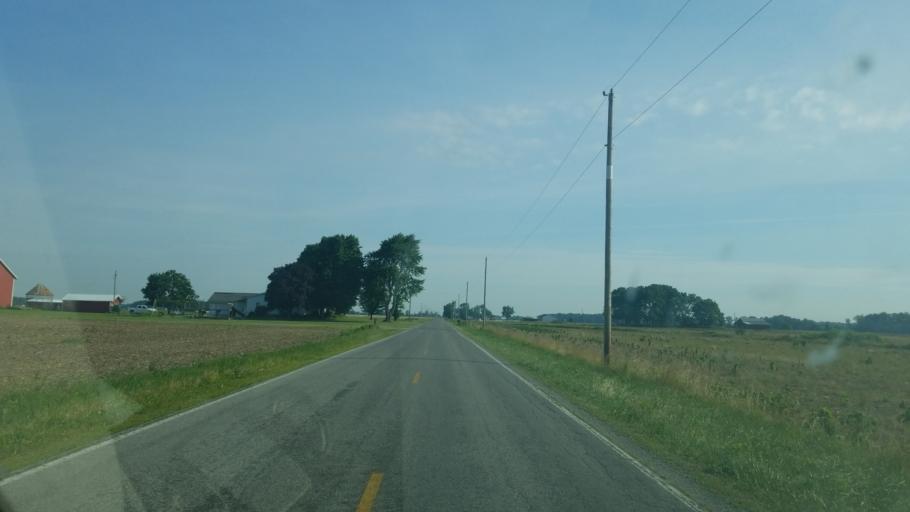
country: US
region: Ohio
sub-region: Hancock County
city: Arlington
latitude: 40.9235
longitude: -83.6986
